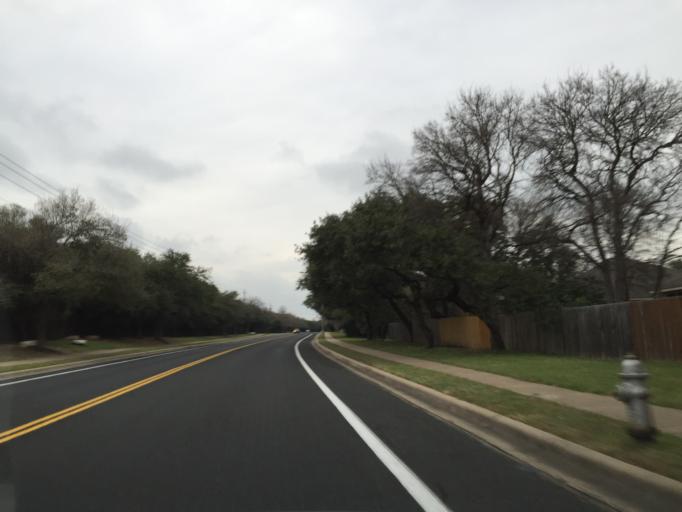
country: US
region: Texas
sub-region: Travis County
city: Barton Creek
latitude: 30.2457
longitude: -97.8384
